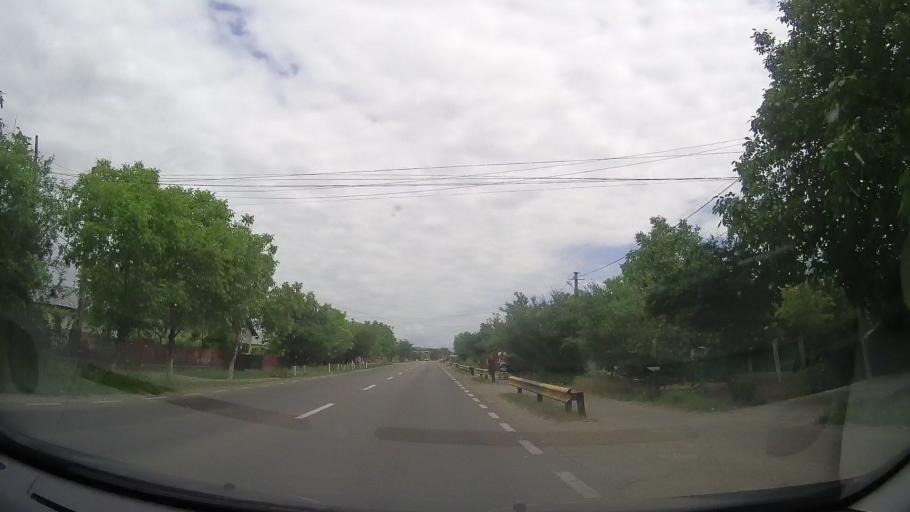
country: RO
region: Prahova
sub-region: Comuna Lipanesti
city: Sipotu
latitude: 45.0342
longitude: 26.0173
